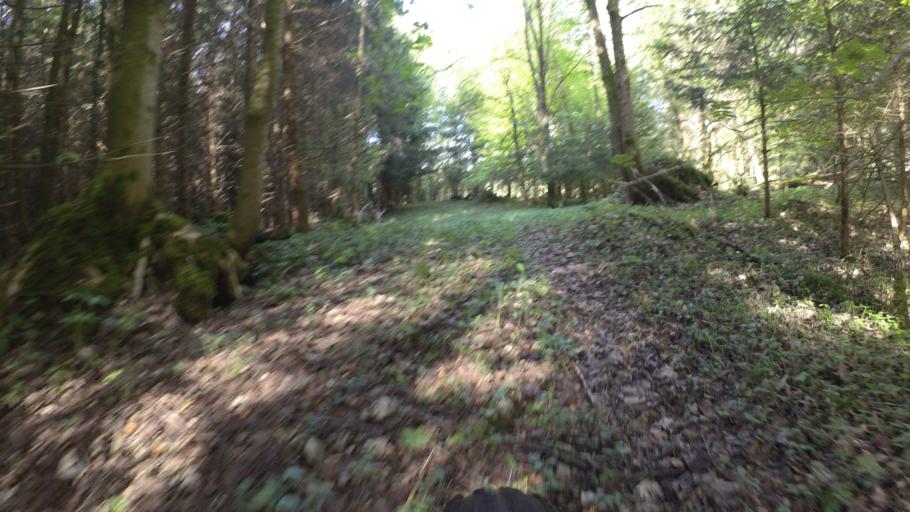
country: DE
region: Bavaria
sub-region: Upper Bavaria
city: Grabenstatt
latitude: 47.8504
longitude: 12.5730
